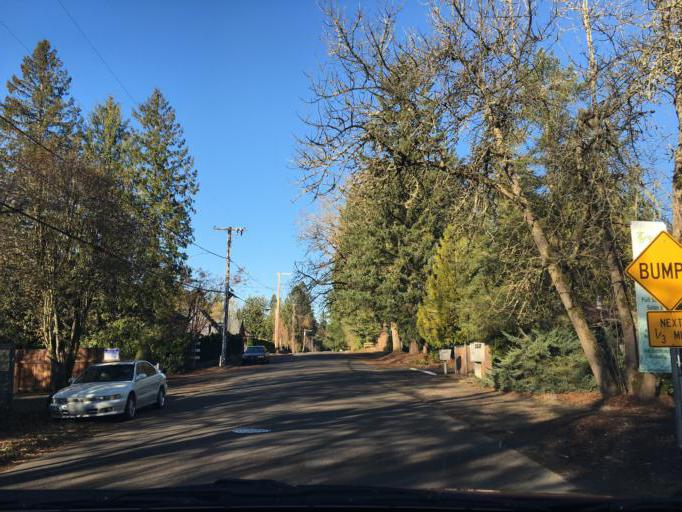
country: US
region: Oregon
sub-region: Washington County
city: Raleigh Hills
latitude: 45.4874
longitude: -122.7758
